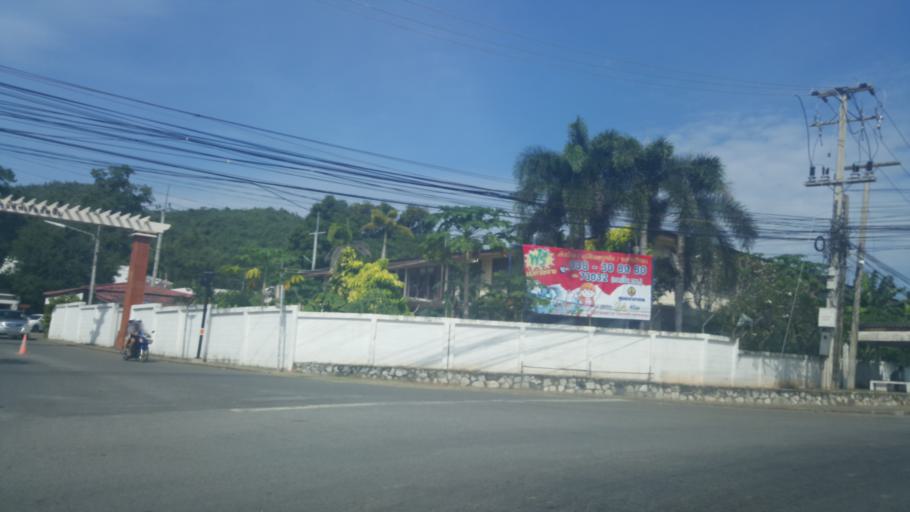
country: TH
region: Chon Buri
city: Sattahip
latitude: 12.6646
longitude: 100.8966
